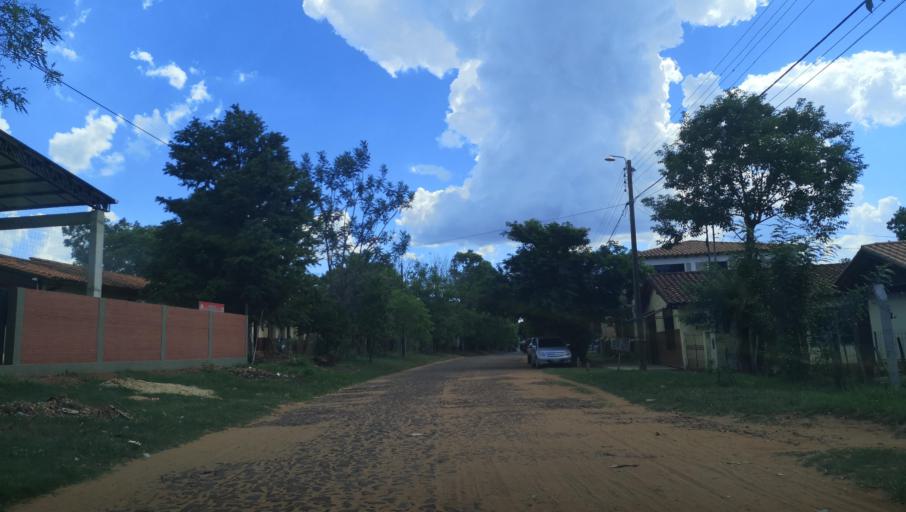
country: PY
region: Misiones
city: Santa Maria
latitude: -26.8888
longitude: -57.0134
